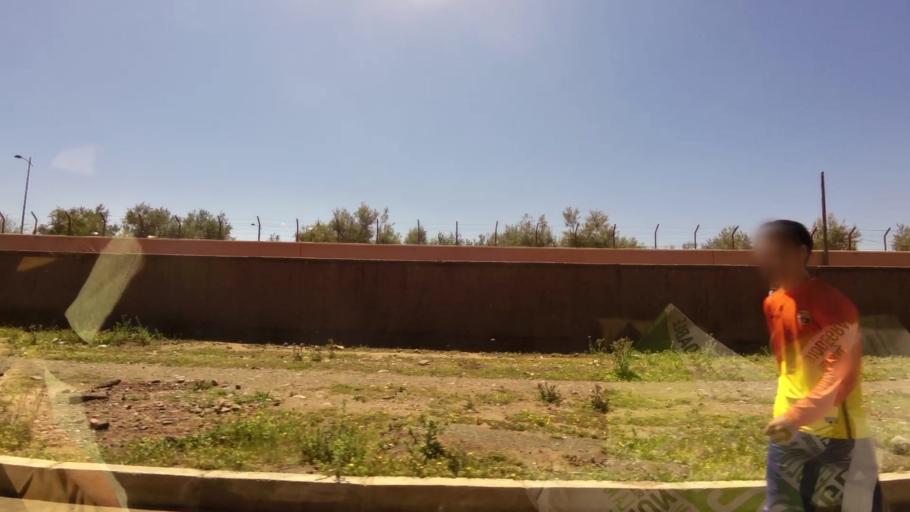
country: MA
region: Marrakech-Tensift-Al Haouz
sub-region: Marrakech
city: Marrakesh
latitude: 31.5509
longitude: -7.9749
